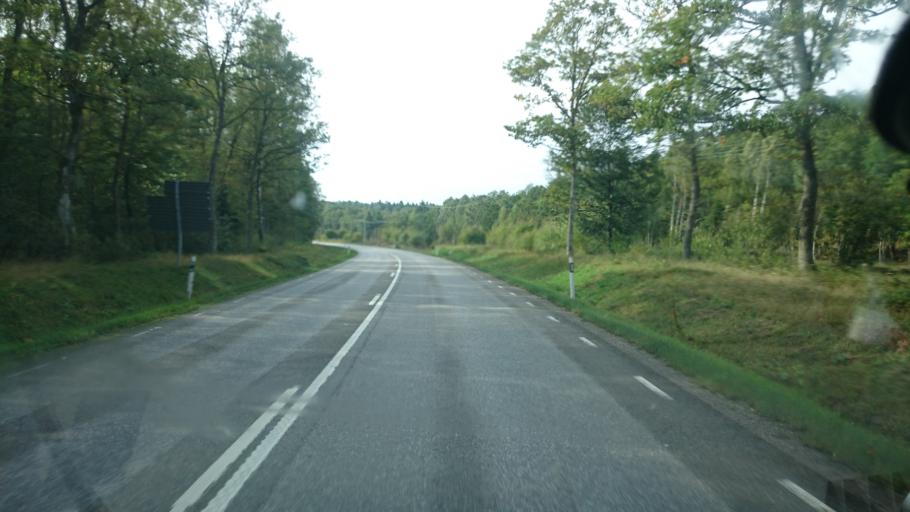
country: SE
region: Vaestra Goetaland
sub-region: Alingsas Kommun
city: Sollebrunn
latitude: 58.0616
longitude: 12.4690
